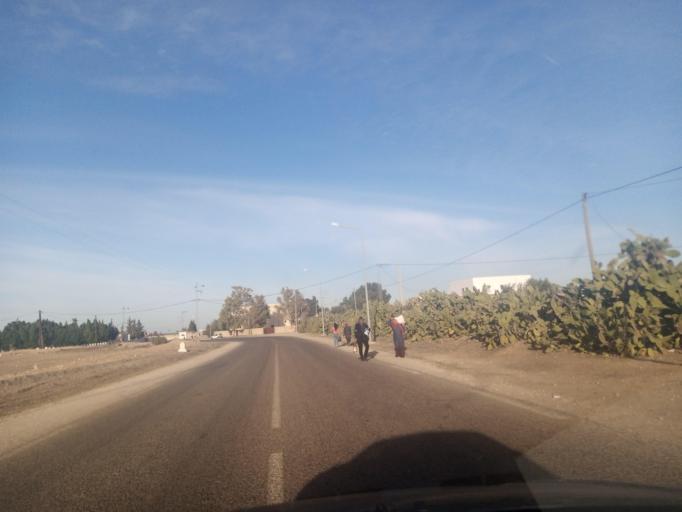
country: TN
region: Al Mahdiyah
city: Shurban
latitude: 34.9589
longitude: 10.3614
